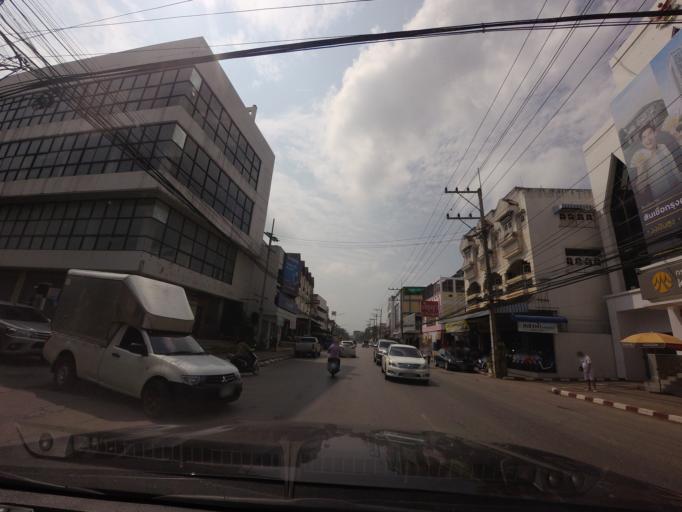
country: TH
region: Phrae
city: Phrae
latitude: 18.1447
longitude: 100.1488
